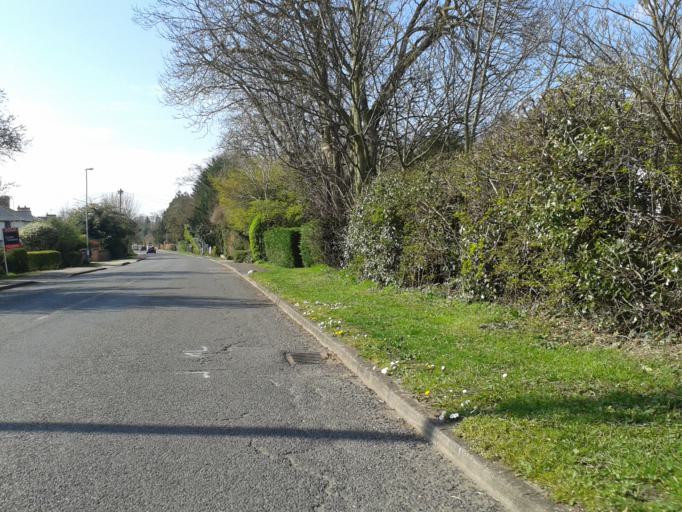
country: GB
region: England
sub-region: Cambridgeshire
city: Sawston
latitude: 52.1547
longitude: 0.1491
